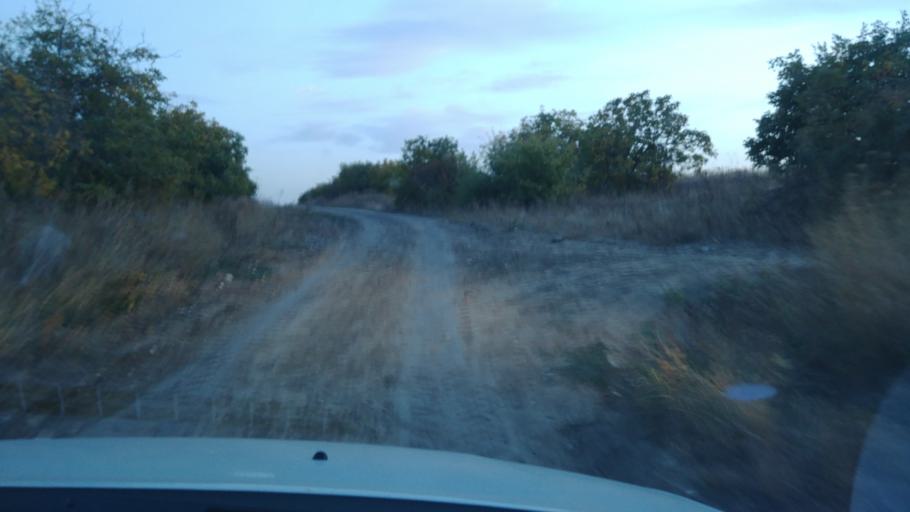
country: MD
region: Rezina
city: Saharna
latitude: 47.6838
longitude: 28.9078
